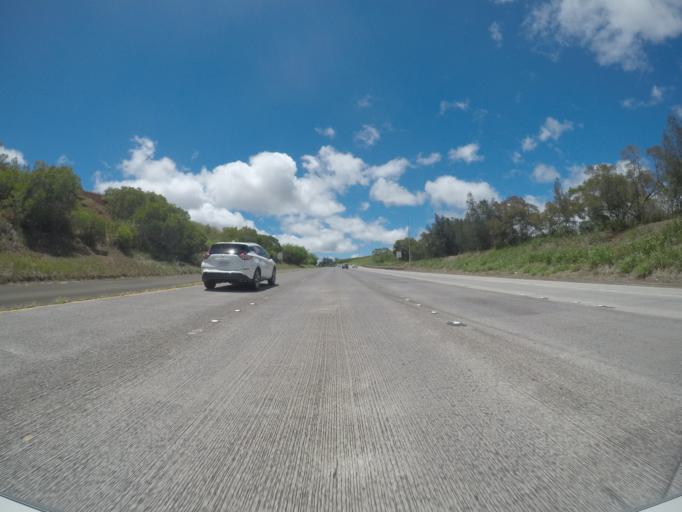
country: US
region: Hawaii
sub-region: Honolulu County
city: Waipio
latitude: 21.4191
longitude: -157.9937
